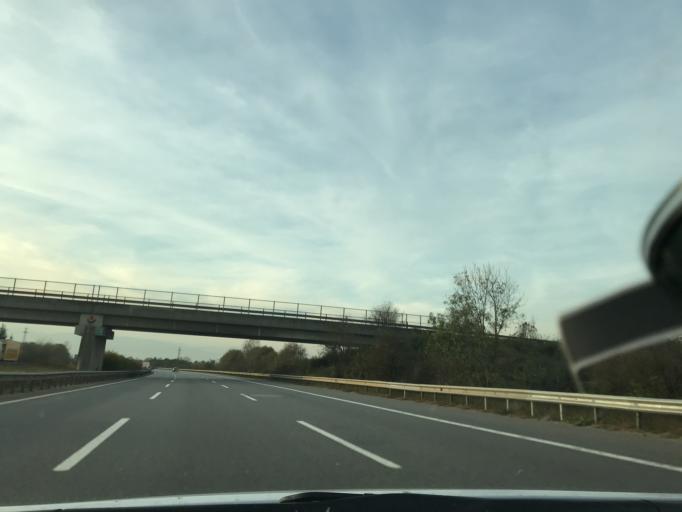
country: TR
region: Duzce
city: Cilimli
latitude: 40.8419
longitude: 31.0235
